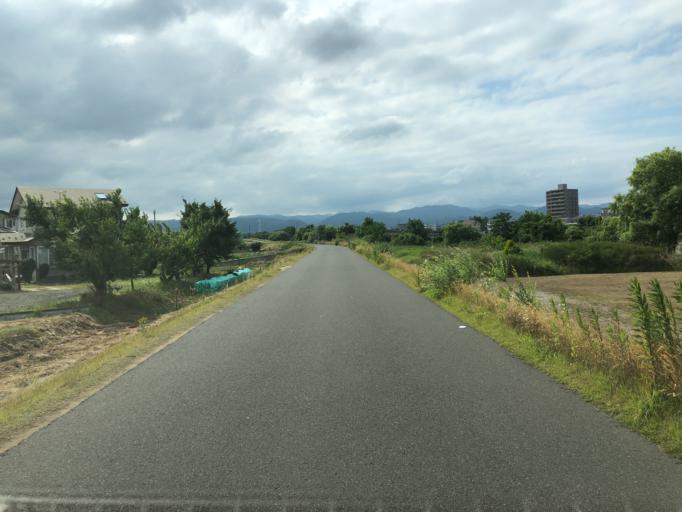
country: JP
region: Fukushima
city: Fukushima-shi
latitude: 37.7519
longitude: 140.4498
